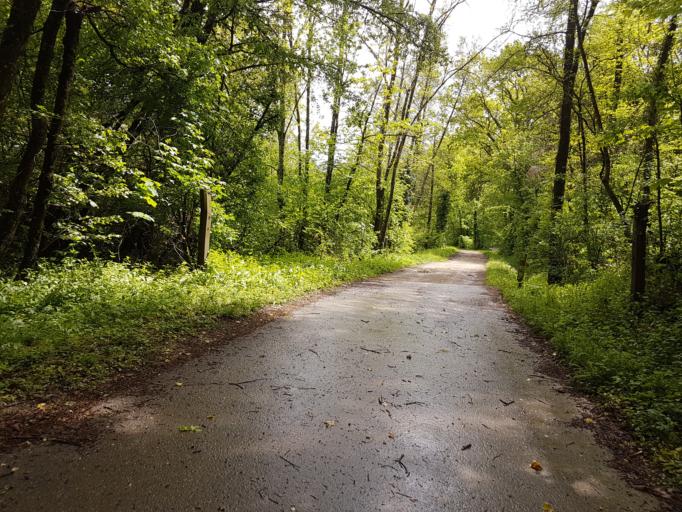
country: CH
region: Vaud
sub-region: Ouest Lausannois District
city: Bussigny
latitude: 46.5498
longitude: 6.5410
